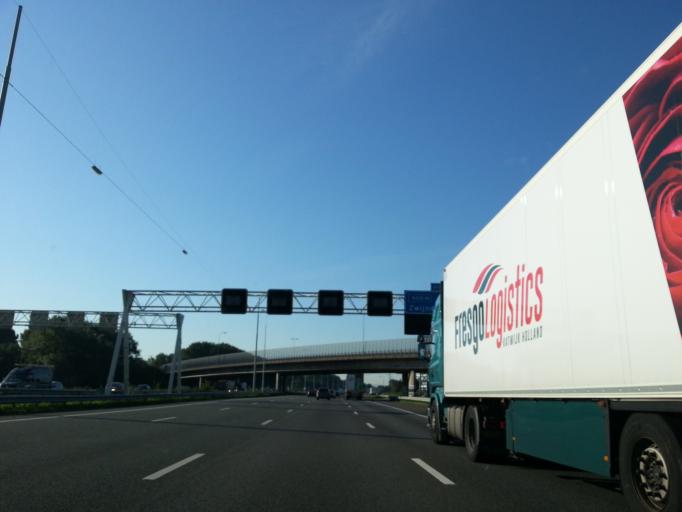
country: NL
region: South Holland
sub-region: Gemeente Zwijndrecht
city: Zwijndrecht
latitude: 51.8326
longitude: 4.6207
